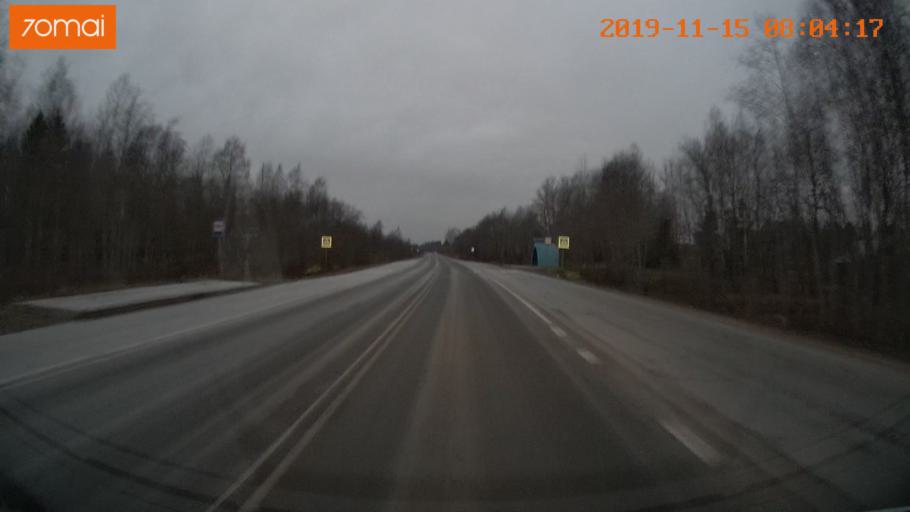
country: RU
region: Vologda
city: Cherepovets
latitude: 59.0062
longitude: 38.0793
